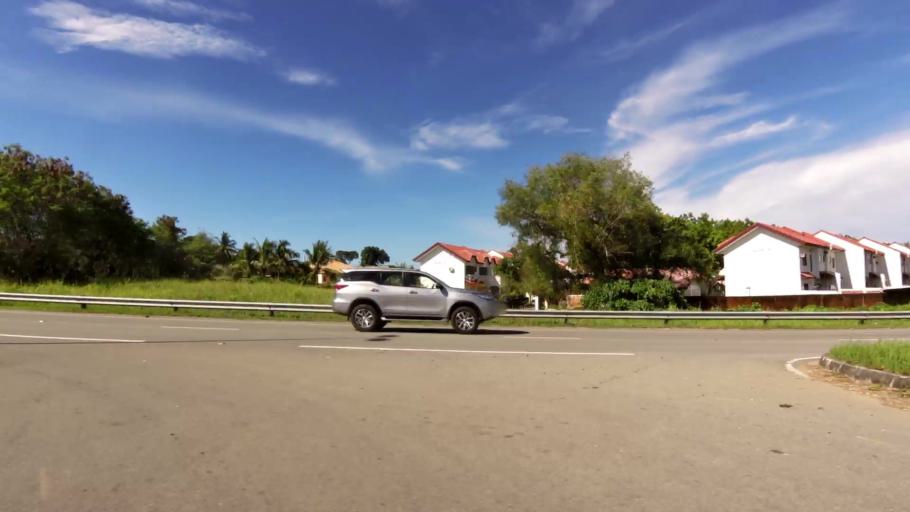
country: BN
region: Brunei and Muara
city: Bandar Seri Begawan
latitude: 4.9664
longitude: 114.9421
